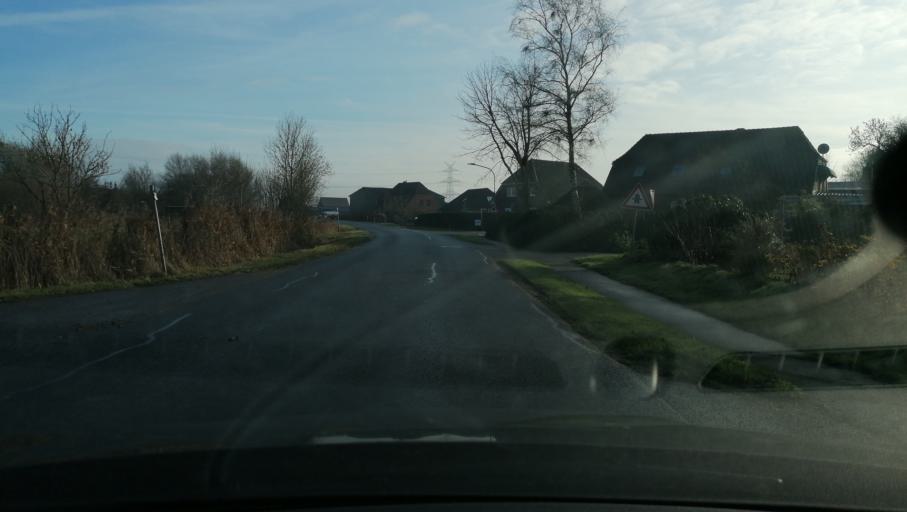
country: DE
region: Schleswig-Holstein
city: Epenwohrden
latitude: 54.1065
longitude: 9.0349
